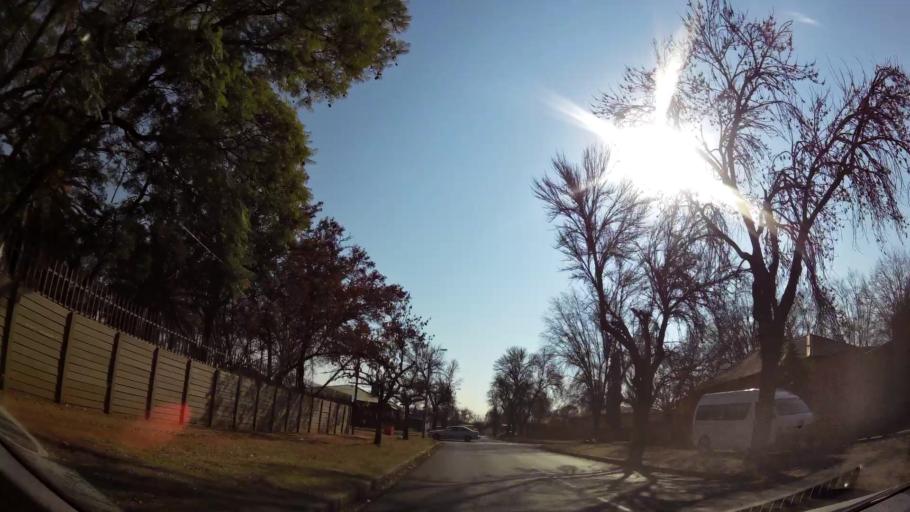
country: ZA
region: Gauteng
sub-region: Ekurhuleni Metropolitan Municipality
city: Boksburg
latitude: -26.2255
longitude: 28.2611
